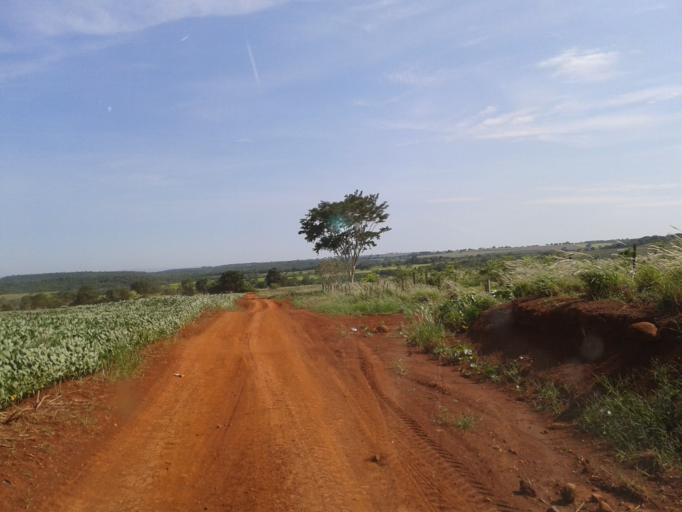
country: BR
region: Minas Gerais
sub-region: Centralina
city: Centralina
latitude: -18.7089
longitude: -49.2052
